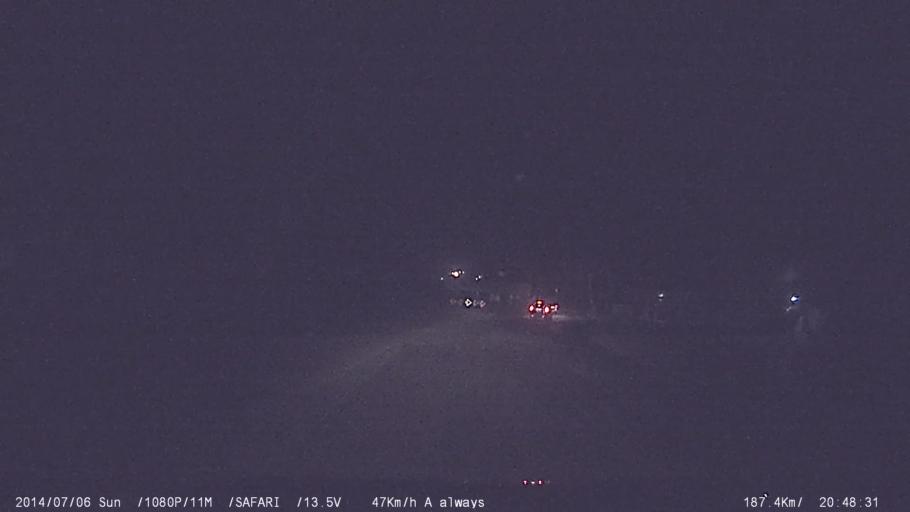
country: IN
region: Tamil Nadu
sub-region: Coimbatore
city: Madukkarai
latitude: 10.8567
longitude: 76.8629
